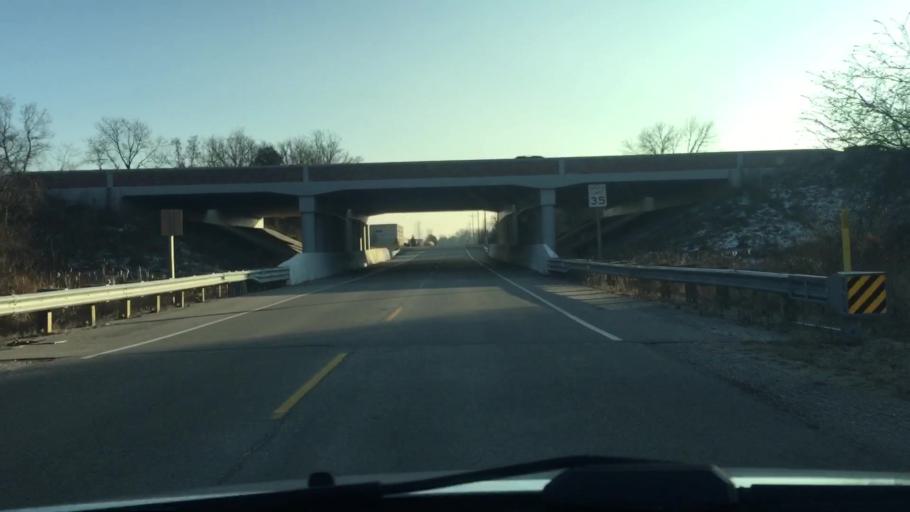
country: US
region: Wisconsin
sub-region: Waukesha County
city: Oconomowoc
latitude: 43.0696
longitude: -88.4812
